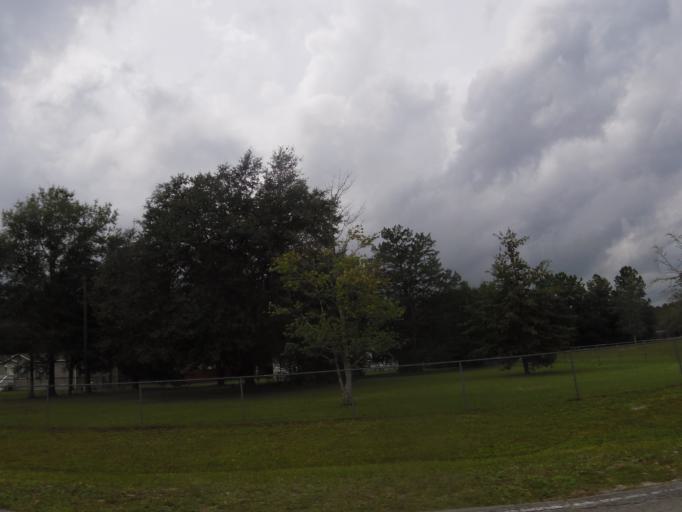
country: US
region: Florida
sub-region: Clay County
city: Middleburg
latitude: 30.1115
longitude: -81.9618
